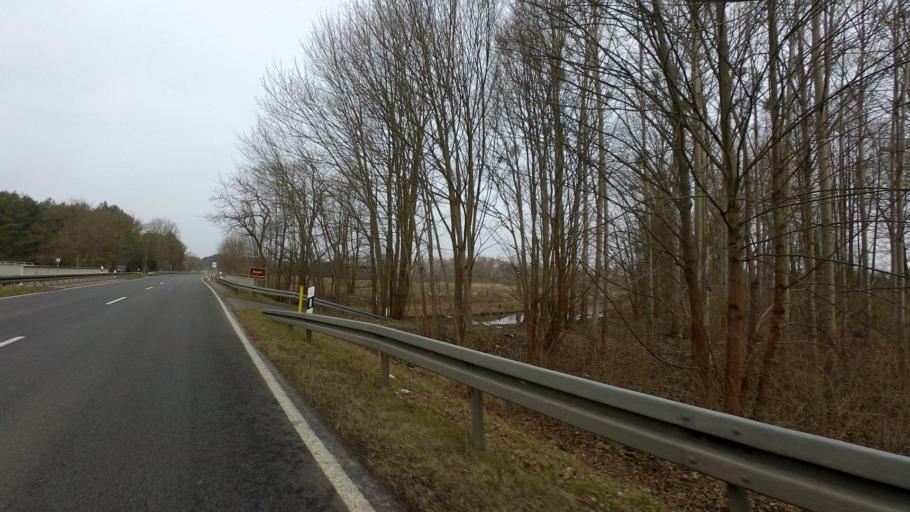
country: DE
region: Brandenburg
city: Michendorf
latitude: 52.2116
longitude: 13.0937
